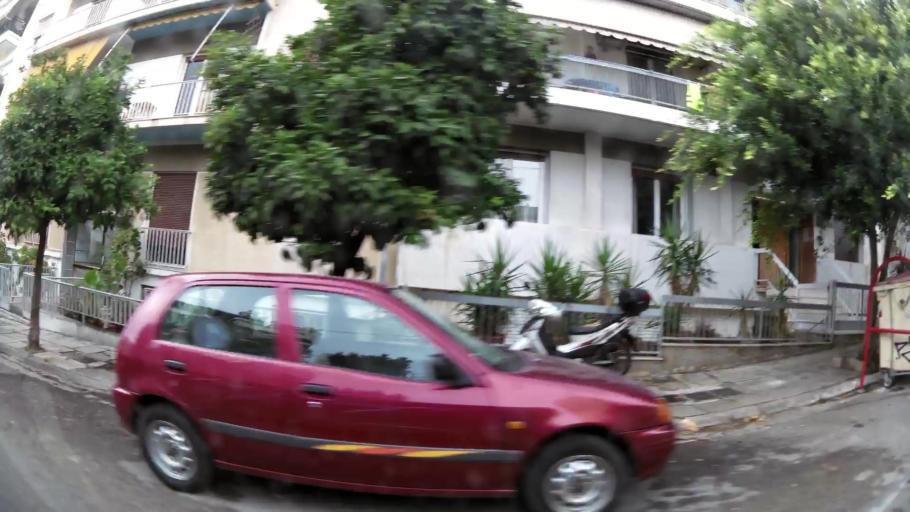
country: GR
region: Attica
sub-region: Nomarchia Athinas
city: Kaisariani
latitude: 37.9540
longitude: 23.7618
